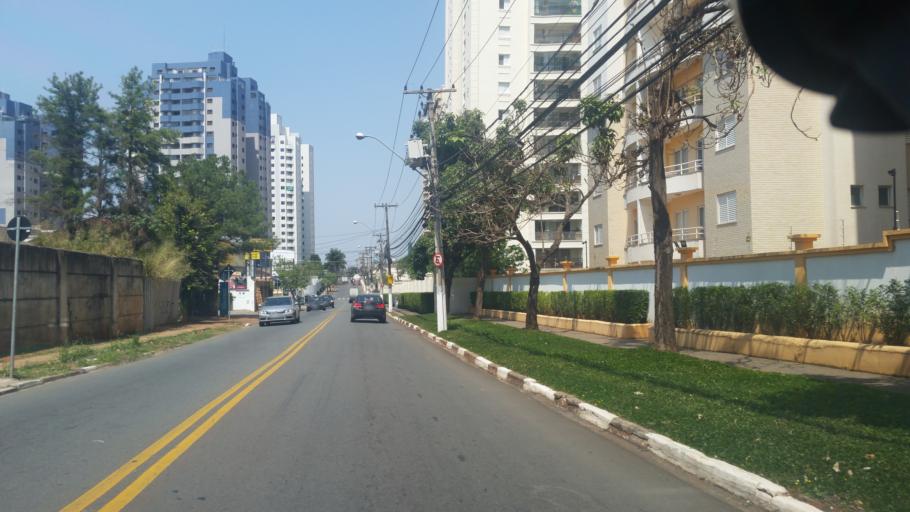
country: BR
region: Sao Paulo
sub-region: Campinas
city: Campinas
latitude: -22.8510
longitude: -47.0536
